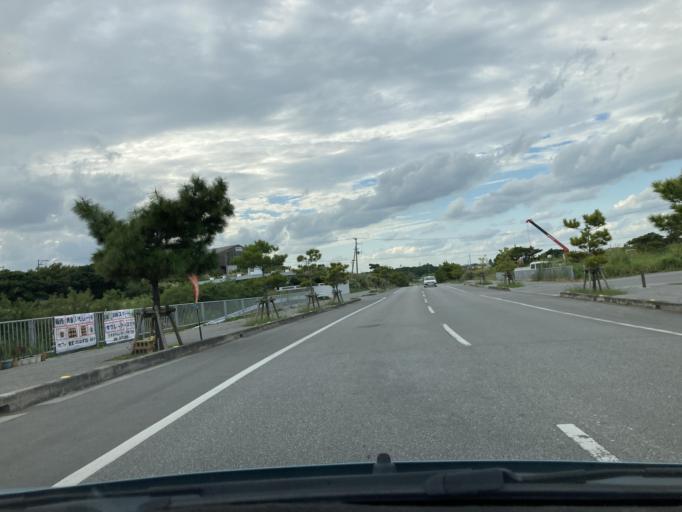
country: JP
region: Okinawa
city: Katsuren-haebaru
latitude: 26.3286
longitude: 127.8921
